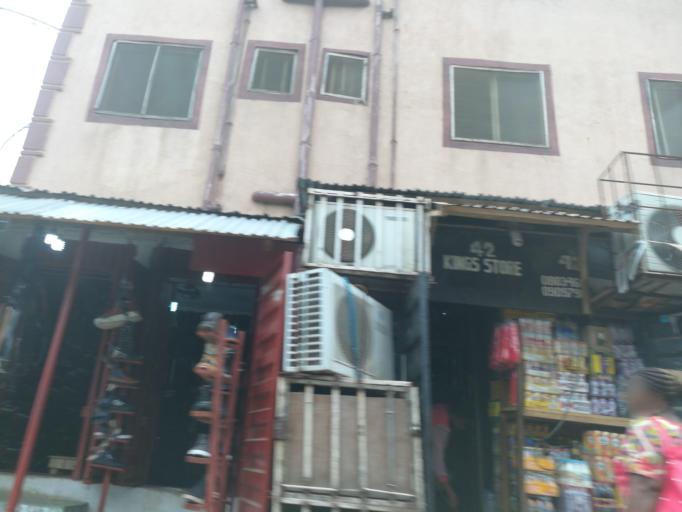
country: NG
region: Lagos
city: Oshodi
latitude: 6.5601
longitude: 3.3477
